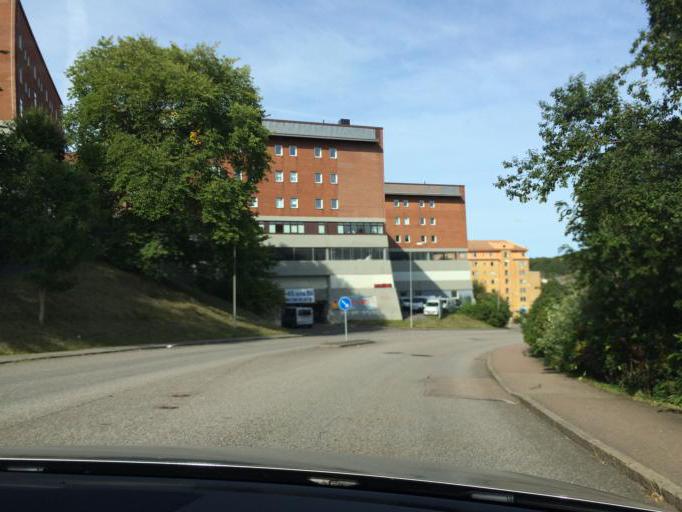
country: SE
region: Vaestra Goetaland
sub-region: Goteborg
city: Goeteborg
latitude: 57.6854
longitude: 11.9945
